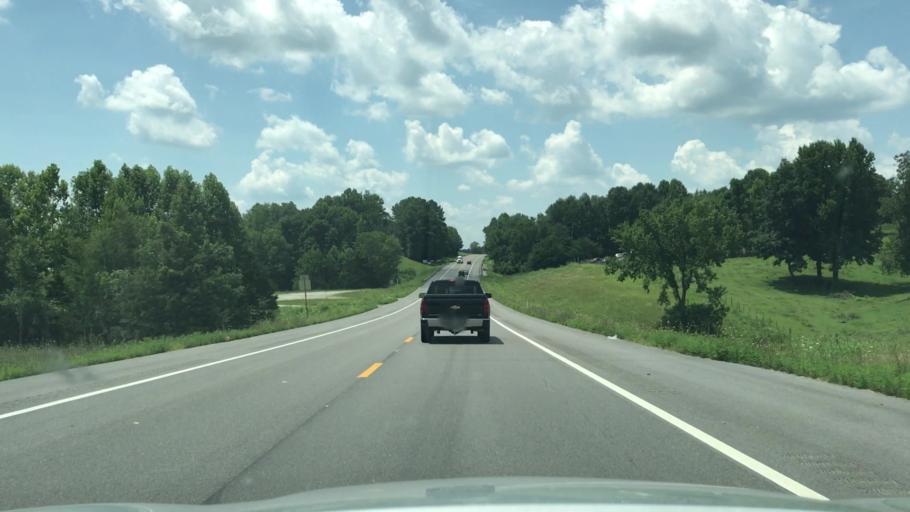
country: US
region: Tennessee
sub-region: Pickett County
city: Byrdstown
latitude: 36.4913
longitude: -85.1816
